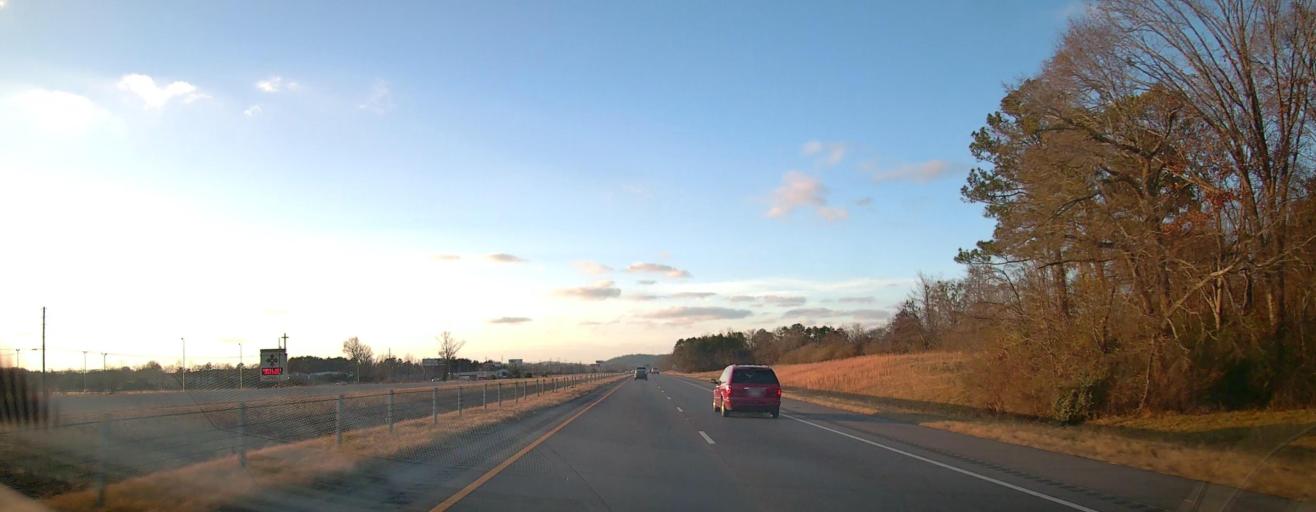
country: US
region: Alabama
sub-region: Etowah County
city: Rainbow City
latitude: 33.9938
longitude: -86.0467
